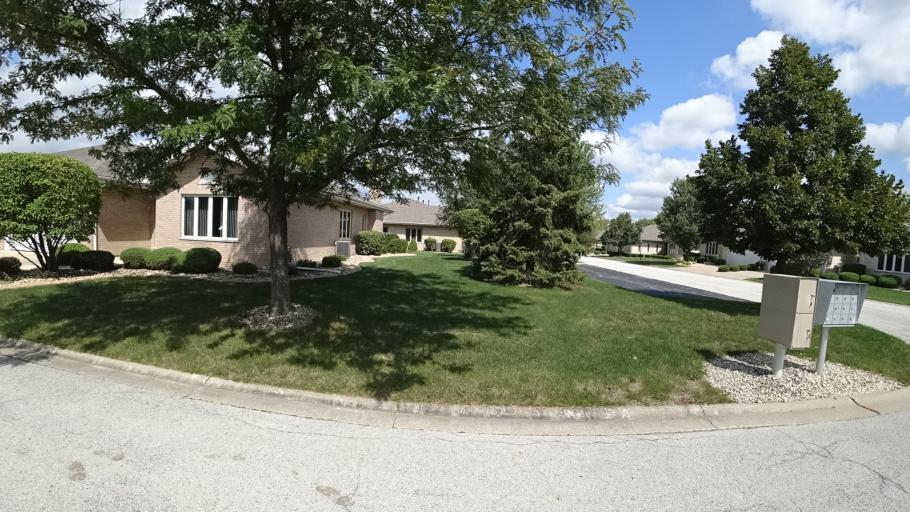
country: US
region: Illinois
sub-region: Cook County
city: Orland Hills
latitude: 41.5703
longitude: -87.8818
